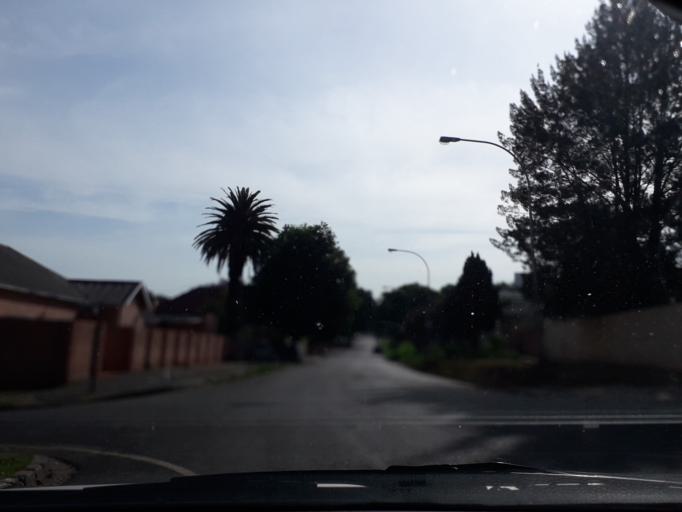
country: ZA
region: Gauteng
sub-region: City of Johannesburg Metropolitan Municipality
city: Johannesburg
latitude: -26.1873
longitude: 28.0769
